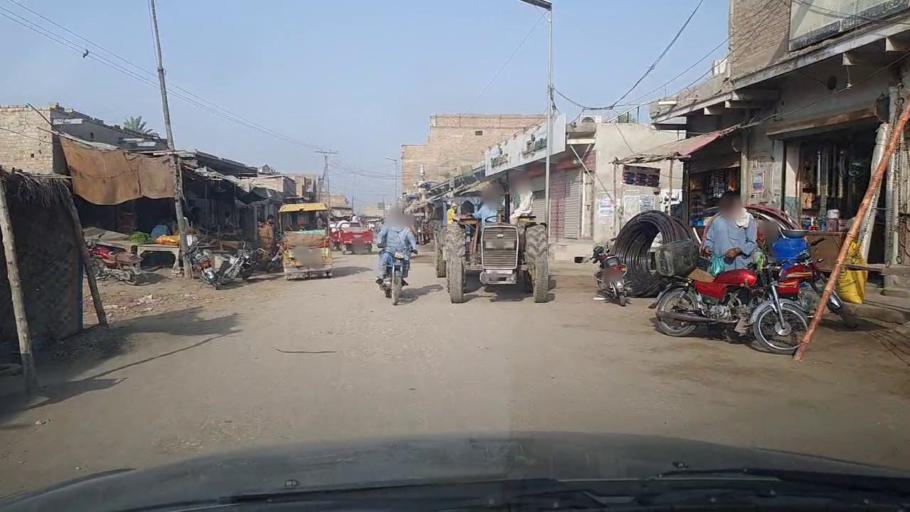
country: PK
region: Sindh
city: Pir jo Goth
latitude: 27.5570
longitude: 68.5584
